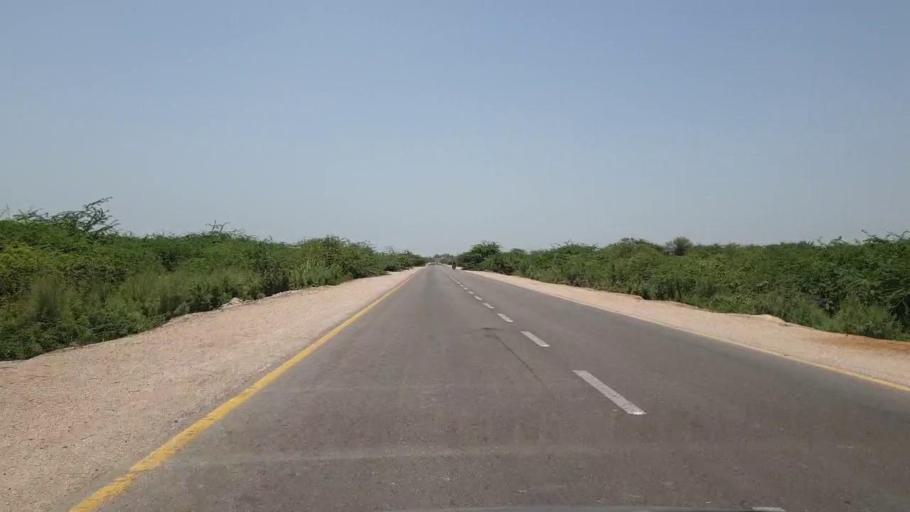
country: PK
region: Sindh
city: Sakrand
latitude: 26.1167
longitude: 68.3861
